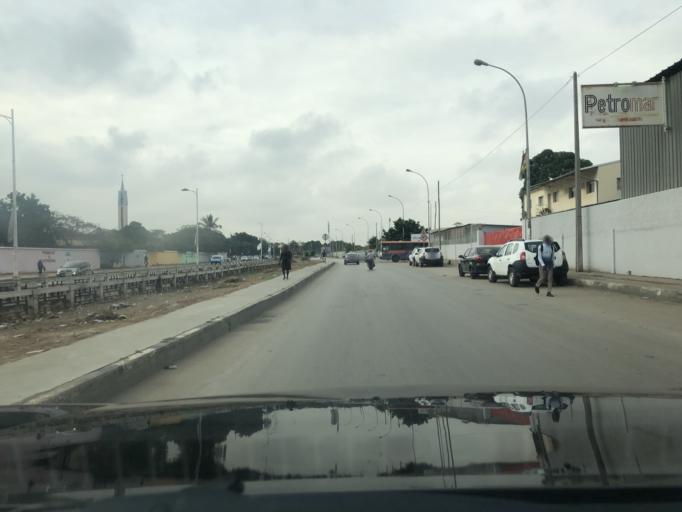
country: AO
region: Luanda
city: Luanda
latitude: -8.8288
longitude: 13.2544
